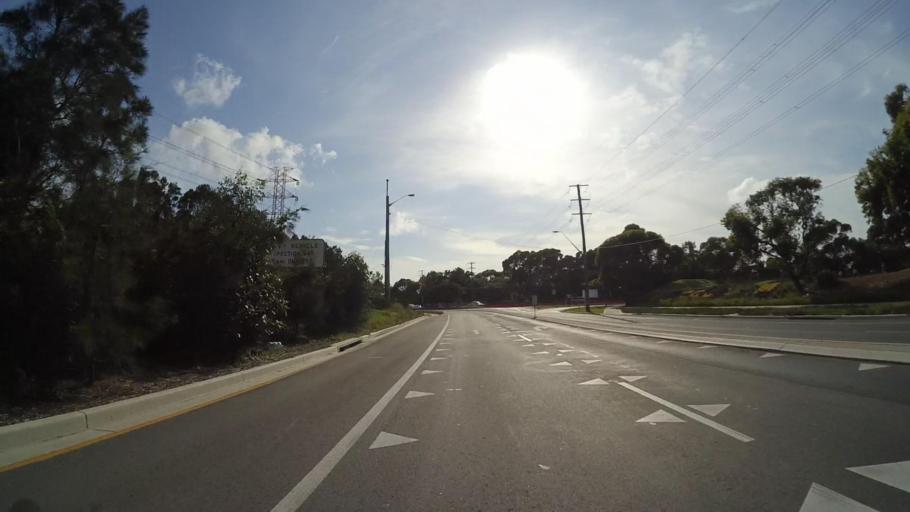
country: AU
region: New South Wales
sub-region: Sutherland Shire
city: Cronulla
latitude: -34.0394
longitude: 151.1555
